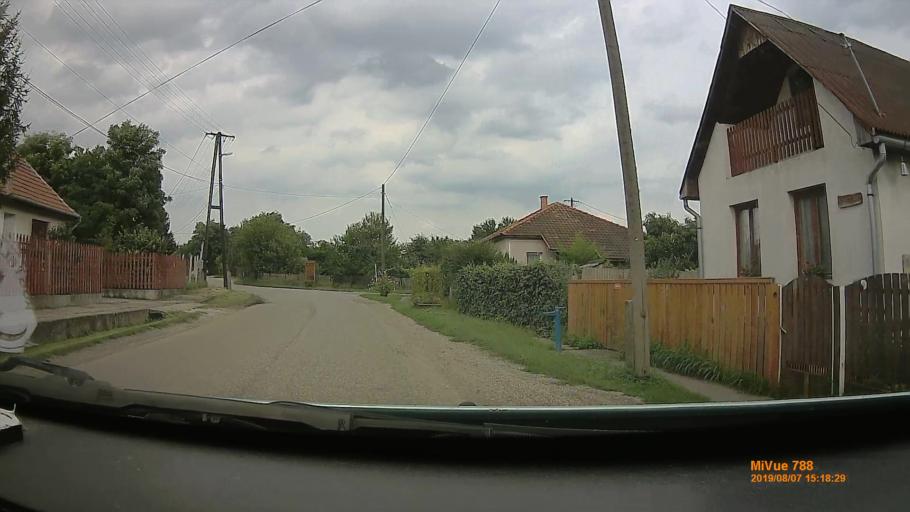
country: HU
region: Borsod-Abauj-Zemplen
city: Encs
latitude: 48.3448
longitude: 21.1393
